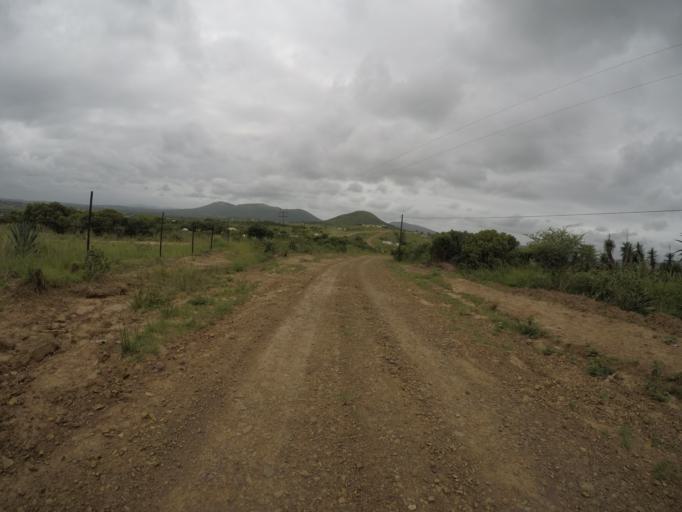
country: ZA
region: KwaZulu-Natal
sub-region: uThungulu District Municipality
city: Empangeni
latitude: -28.6034
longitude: 31.8368
